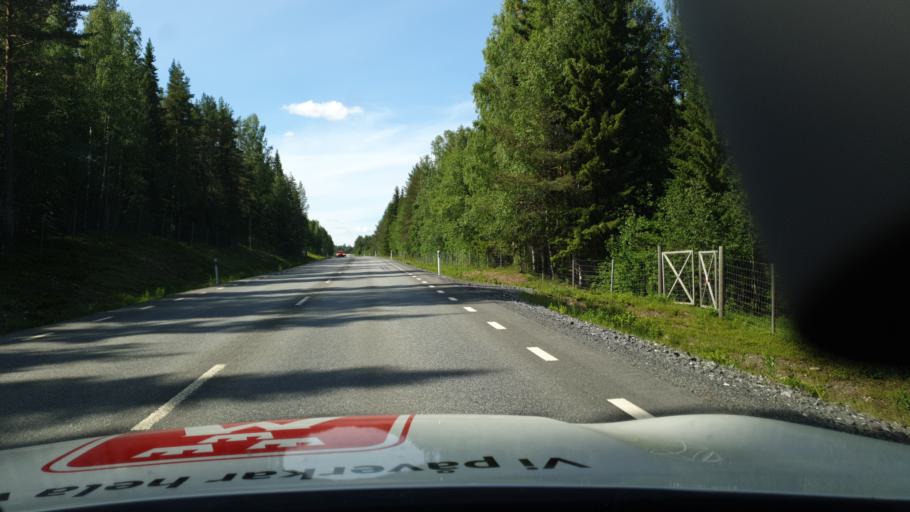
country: SE
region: Vaesterbotten
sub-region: Skelleftea Kommun
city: Forsbacka
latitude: 64.8544
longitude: 20.4799
